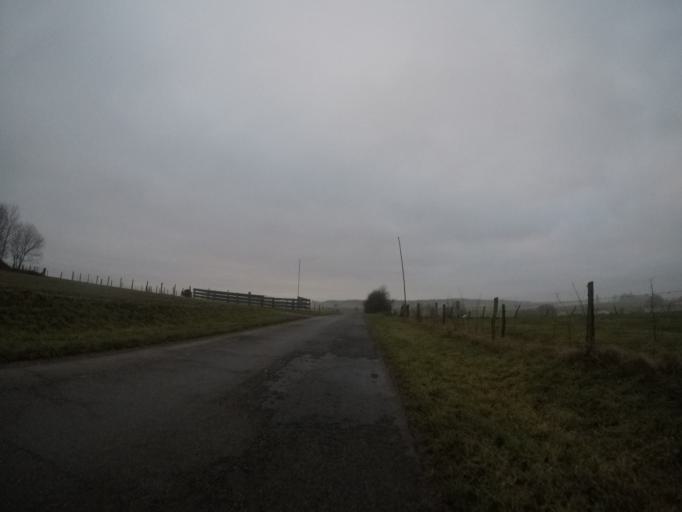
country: BE
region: Wallonia
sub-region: Province du Luxembourg
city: Leglise
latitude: 49.7825
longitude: 5.5584
